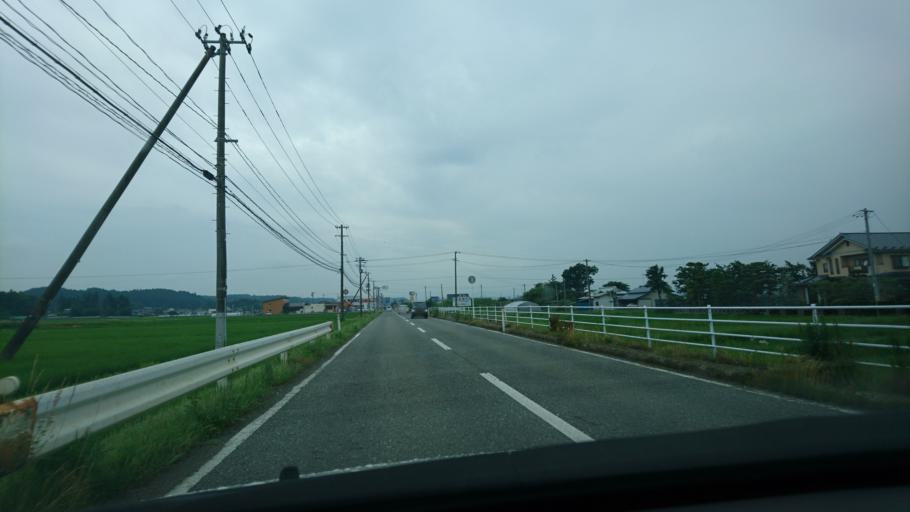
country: JP
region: Miyagi
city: Furukawa
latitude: 38.7333
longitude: 140.9637
